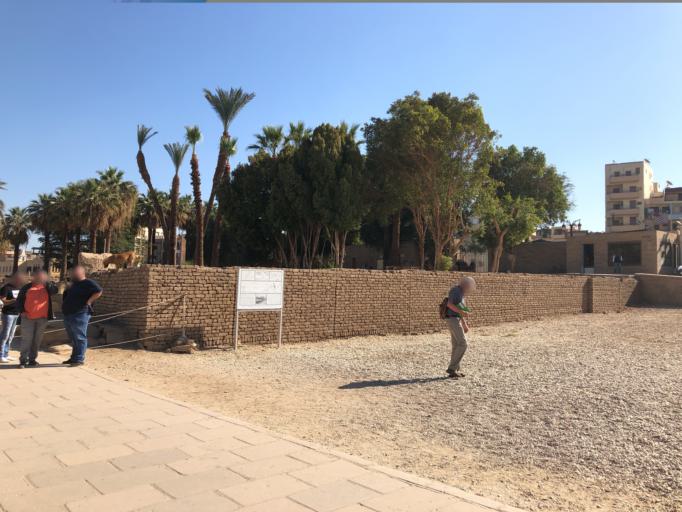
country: EG
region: Luxor
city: Luxor
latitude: 25.7006
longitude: 32.6401
